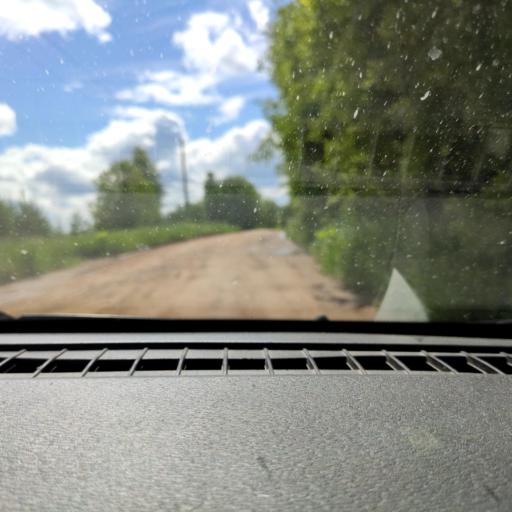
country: RU
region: Perm
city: Overyata
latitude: 58.1311
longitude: 55.8256
